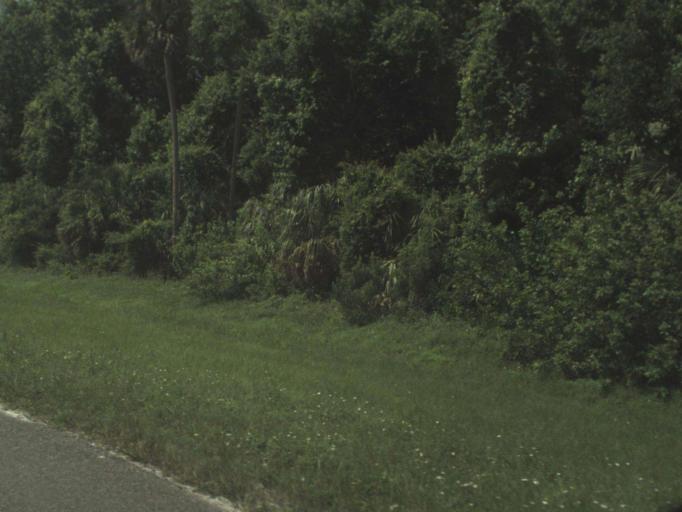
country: US
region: Florida
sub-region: Orange County
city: Christmas
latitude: 28.3924
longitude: -80.9417
